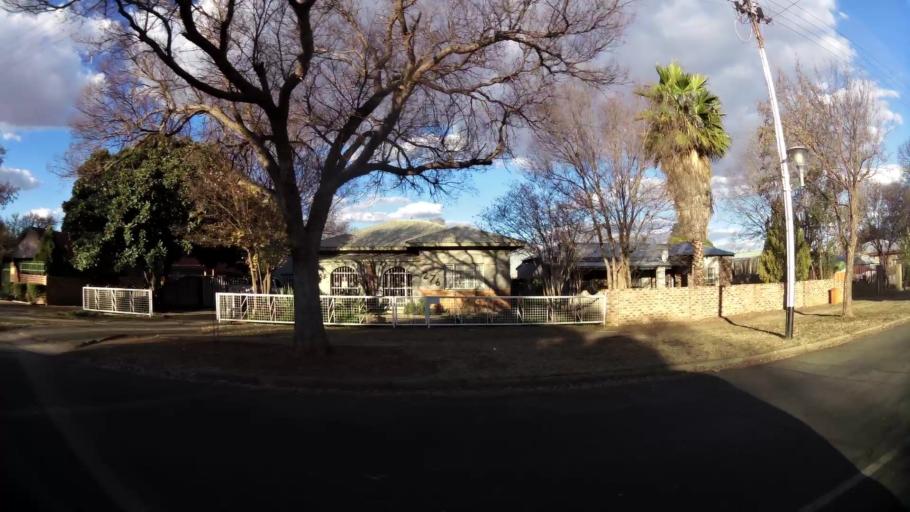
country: ZA
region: North-West
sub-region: Dr Kenneth Kaunda District Municipality
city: Potchefstroom
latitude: -26.7366
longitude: 27.0890
